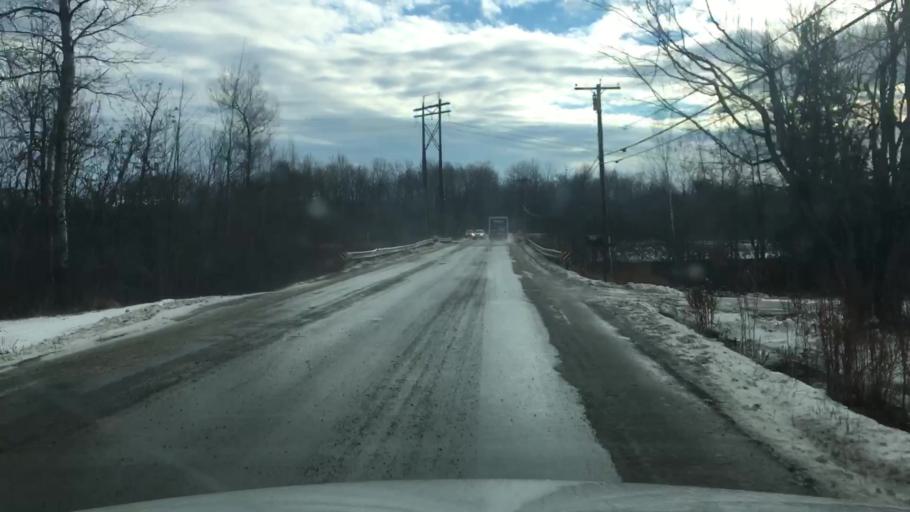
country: US
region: Maine
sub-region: Penobscot County
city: Brewer
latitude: 44.7302
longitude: -68.7576
